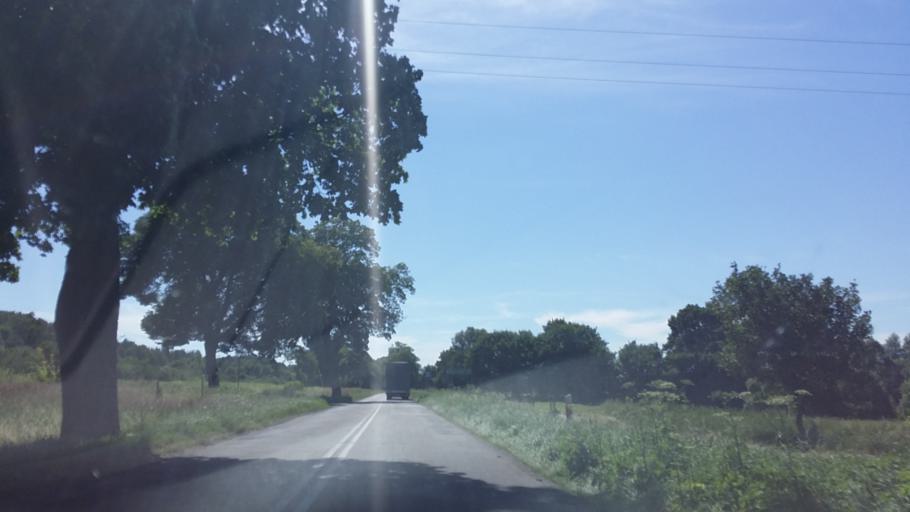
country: PL
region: West Pomeranian Voivodeship
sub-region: Powiat lobeski
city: Lobez
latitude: 53.6497
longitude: 15.6405
